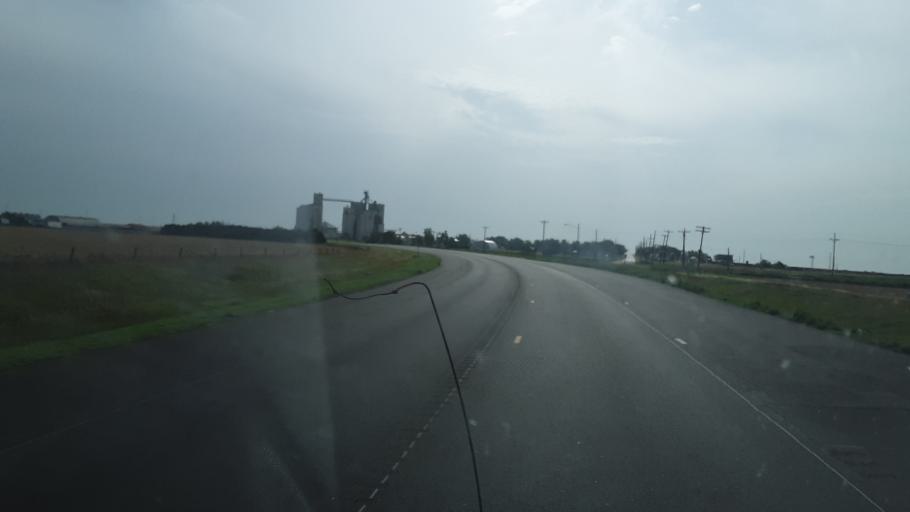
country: US
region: Kansas
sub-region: Ford County
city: Dodge City
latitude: 37.7789
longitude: -99.9011
